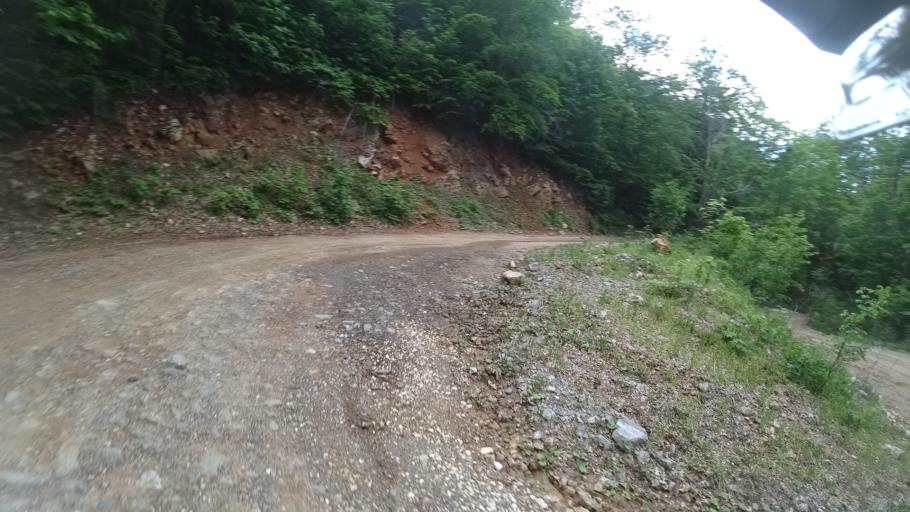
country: HR
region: Licko-Senjska
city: Gospic
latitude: 44.4633
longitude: 15.2983
